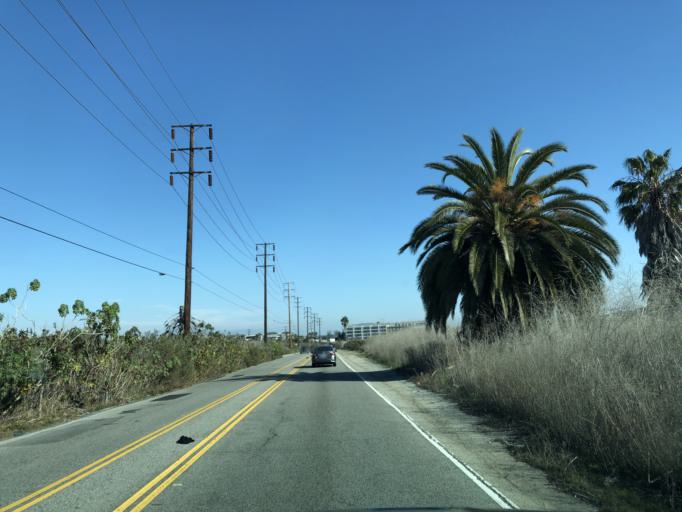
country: US
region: California
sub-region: Los Angeles County
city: Marina del Rey
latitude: 33.9705
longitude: -118.4370
